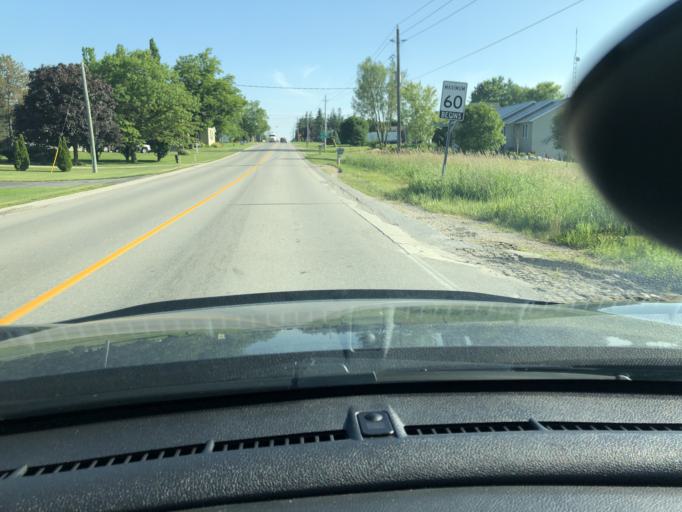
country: CA
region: Ontario
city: Stratford
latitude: 43.4229
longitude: -80.8381
